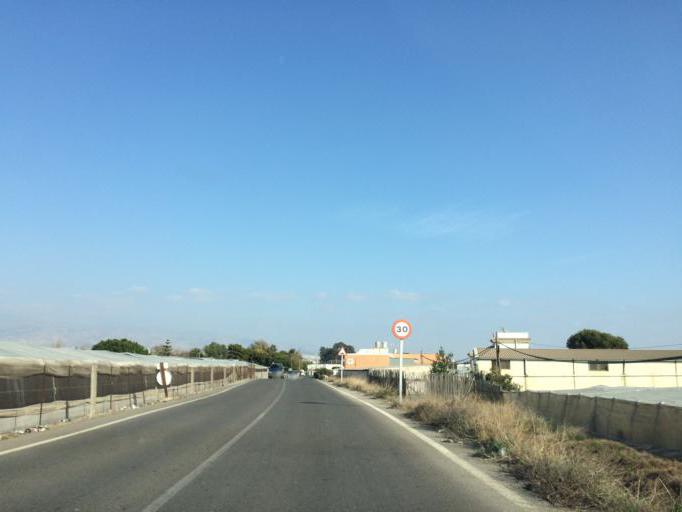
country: ES
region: Andalusia
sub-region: Provincia de Almeria
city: Almeria
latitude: 36.8443
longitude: -2.4265
